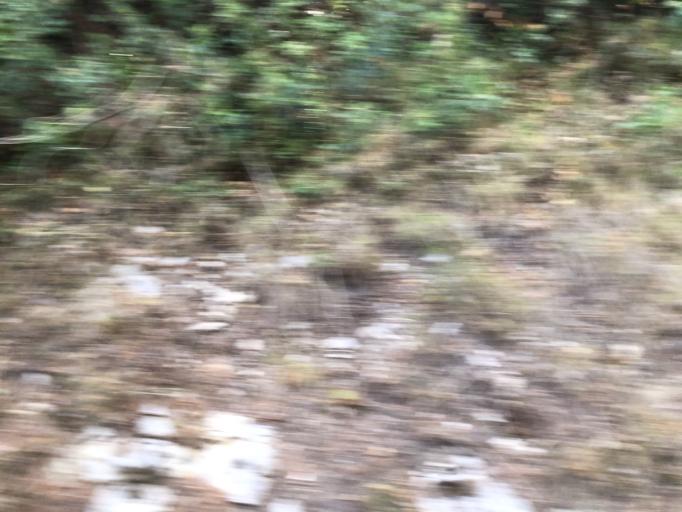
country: FR
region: Provence-Alpes-Cote d'Azur
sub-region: Departement des Alpes-Maritimes
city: Beaulieu-sur-Mer
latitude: 43.7102
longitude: 7.3226
